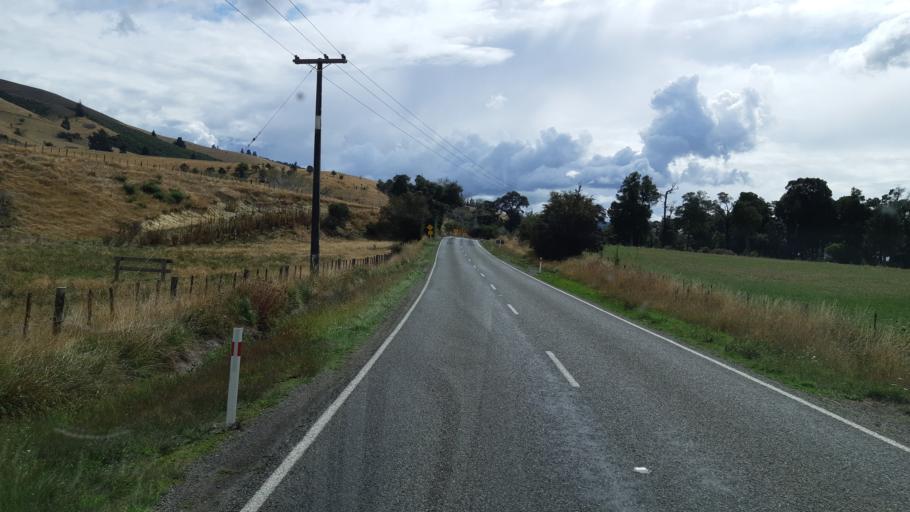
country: NZ
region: Tasman
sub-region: Tasman District
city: Wakefield
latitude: -41.5086
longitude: 172.7951
